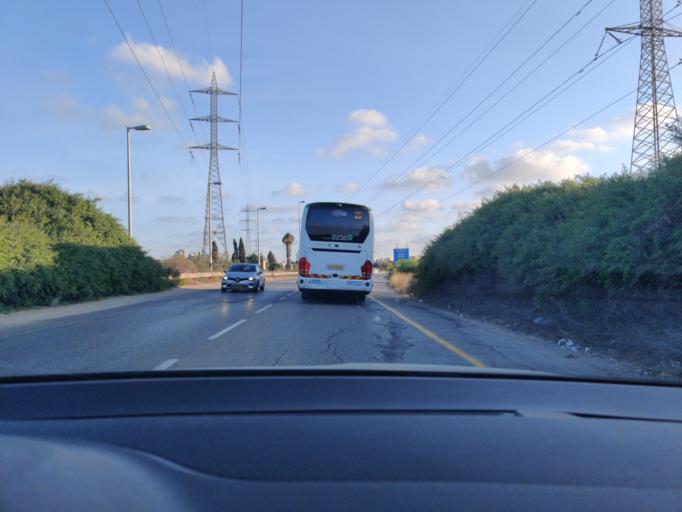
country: IL
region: Haifa
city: Hadera
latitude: 32.4446
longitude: 34.9392
